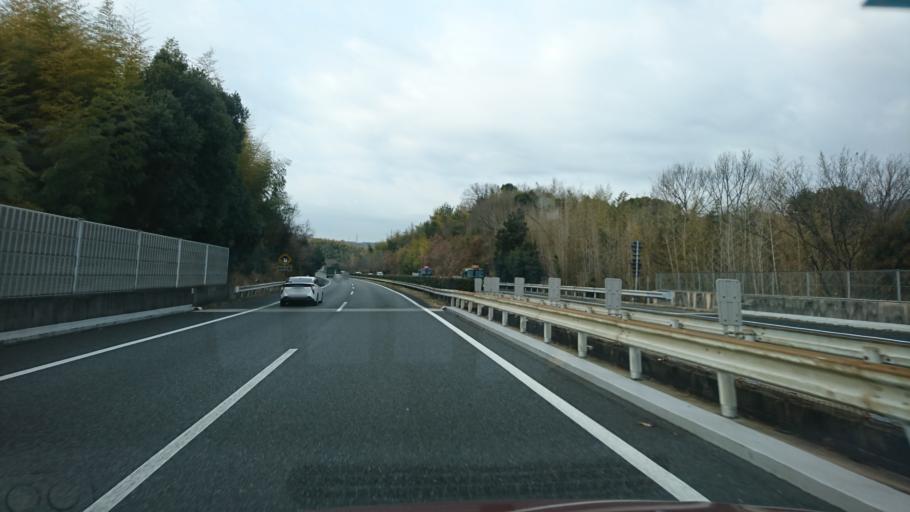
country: JP
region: Okayama
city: Kurashiki
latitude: 34.6044
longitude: 133.7111
